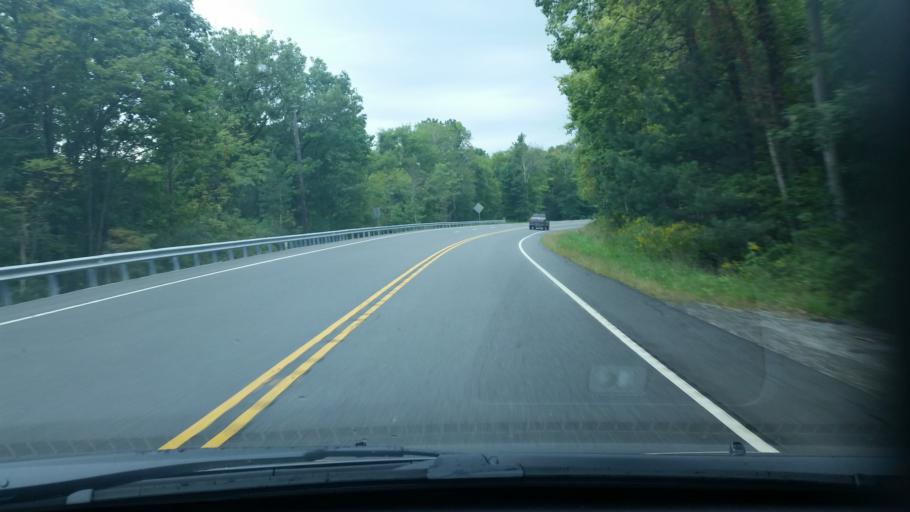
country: US
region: Pennsylvania
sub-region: Clearfield County
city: Shiloh
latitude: 41.0659
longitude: -78.3138
